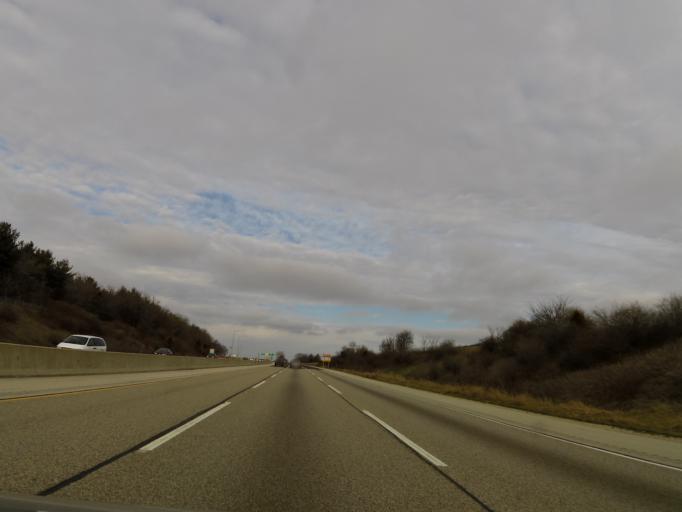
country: US
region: Illinois
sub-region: Winnebago County
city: Roscoe
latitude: 42.3586
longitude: -88.9641
